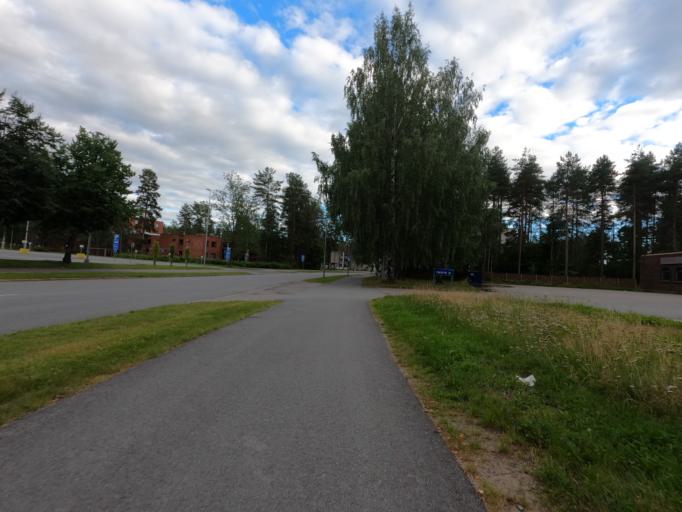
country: FI
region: North Karelia
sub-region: Joensuu
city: Joensuu
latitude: 62.6144
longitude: 29.8133
